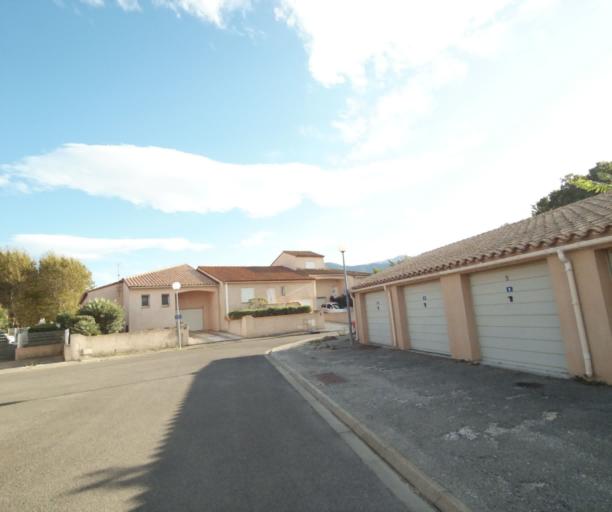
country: FR
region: Languedoc-Roussillon
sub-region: Departement des Pyrenees-Orientales
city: Argelers
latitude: 42.5492
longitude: 3.0380
